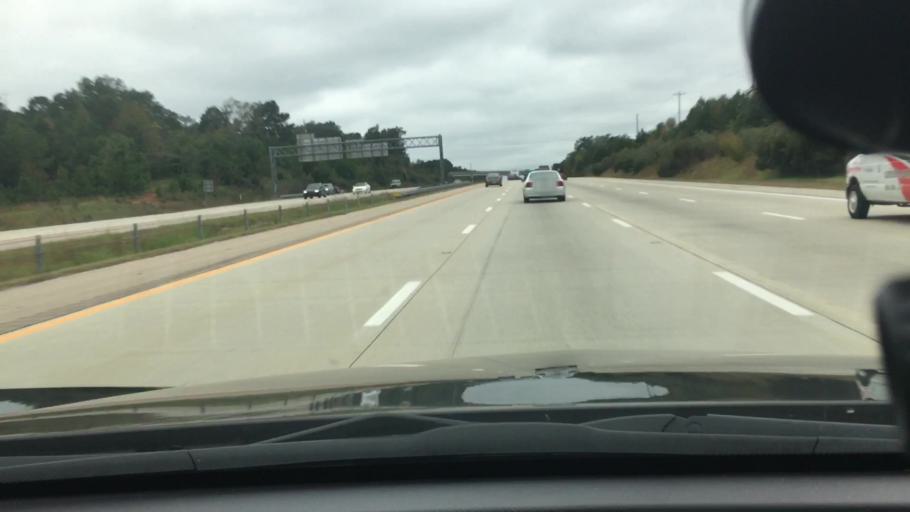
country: US
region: North Carolina
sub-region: Wake County
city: Knightdale
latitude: 35.7679
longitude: -78.5144
